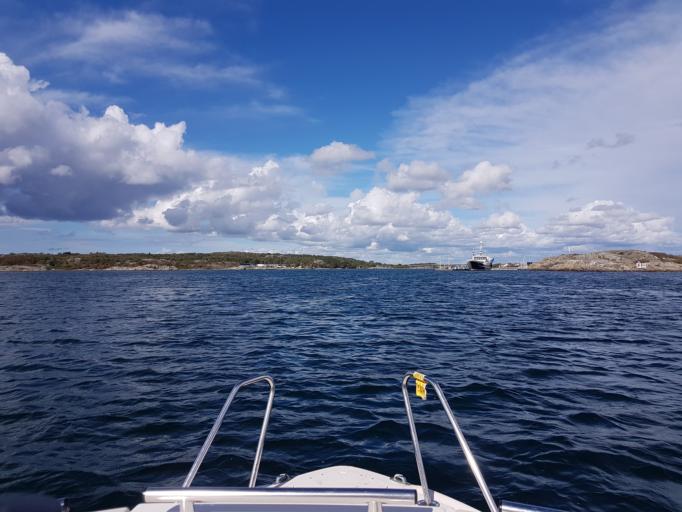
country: SE
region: Vaestra Goetaland
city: Donso
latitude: 57.5936
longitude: 11.7852
